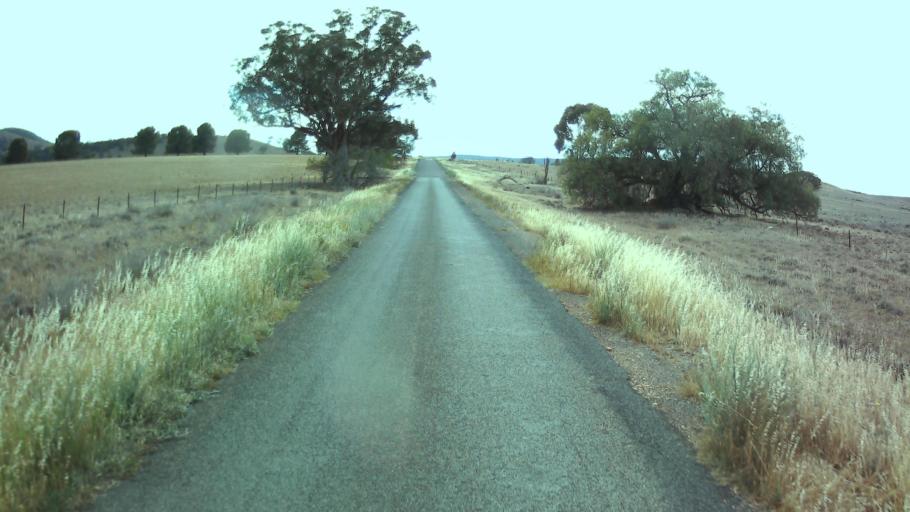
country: AU
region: New South Wales
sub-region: Weddin
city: Grenfell
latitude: -33.8454
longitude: 148.2494
